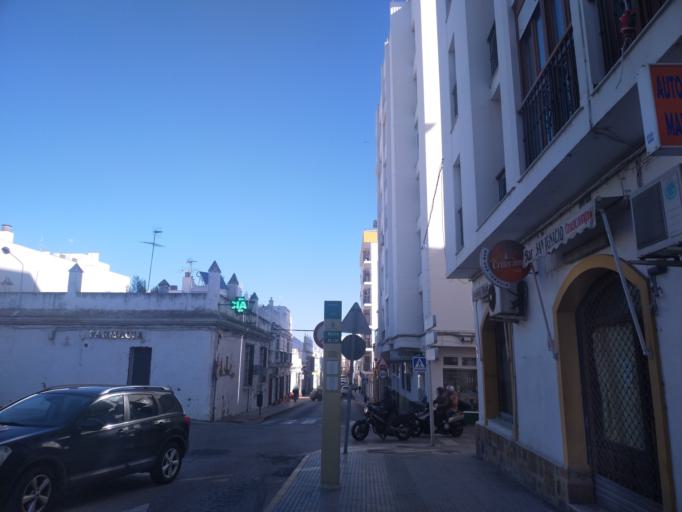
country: ES
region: Andalusia
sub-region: Provincia de Cadiz
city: San Fernando
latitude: 36.4707
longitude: -6.1977
